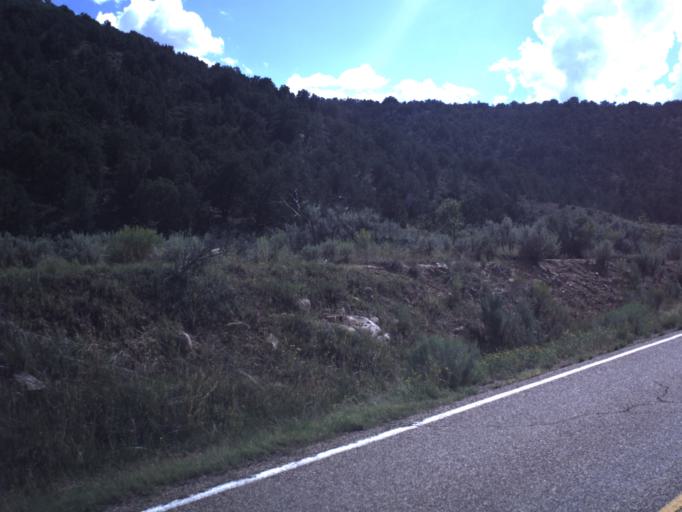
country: US
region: Utah
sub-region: Duchesne County
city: Duchesne
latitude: 40.3230
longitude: -110.6759
